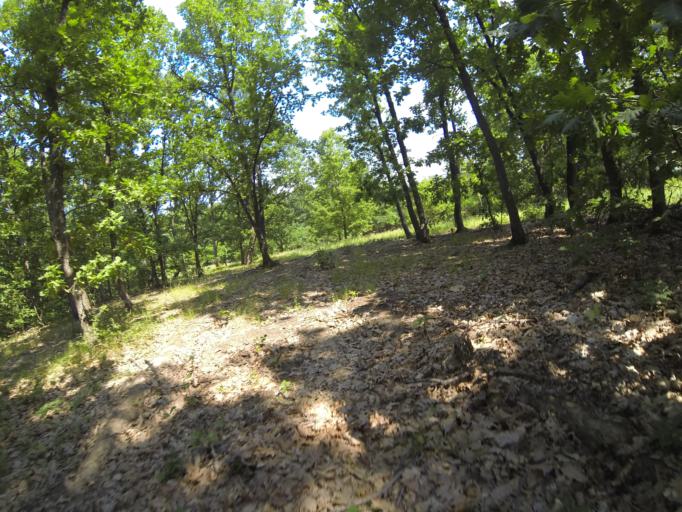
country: RO
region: Gorj
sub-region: Comuna Crusetu
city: Crusetu
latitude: 44.6141
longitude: 23.6409
